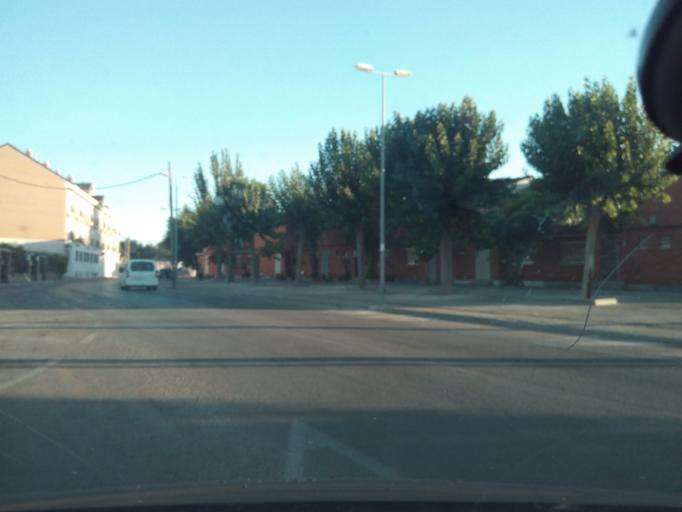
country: ES
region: Castille-La Mancha
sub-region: Province of Toledo
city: Villacanas
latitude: 39.6176
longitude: -3.3394
